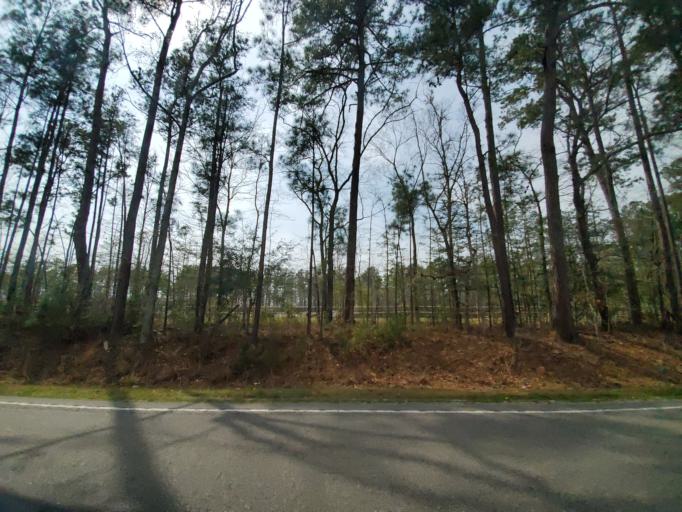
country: US
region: South Carolina
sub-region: Dorchester County
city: Ridgeville
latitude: 32.9902
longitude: -80.3076
